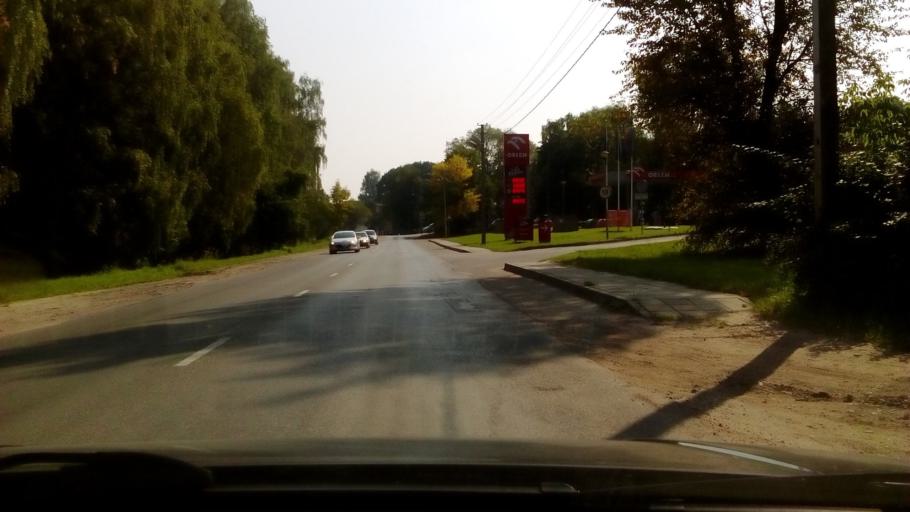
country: LT
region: Alytaus apskritis
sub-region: Alytus
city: Alytus
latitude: 54.4040
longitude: 24.0367
